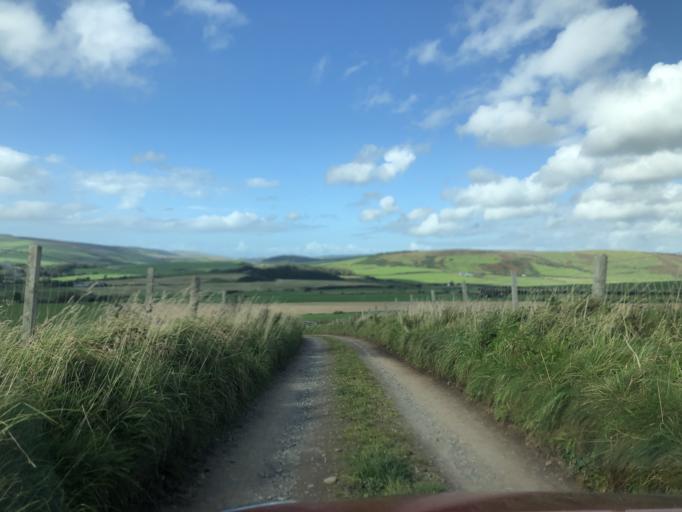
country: GB
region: Scotland
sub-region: Argyll and Bute
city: Campbeltown
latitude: 55.3151
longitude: -5.6095
